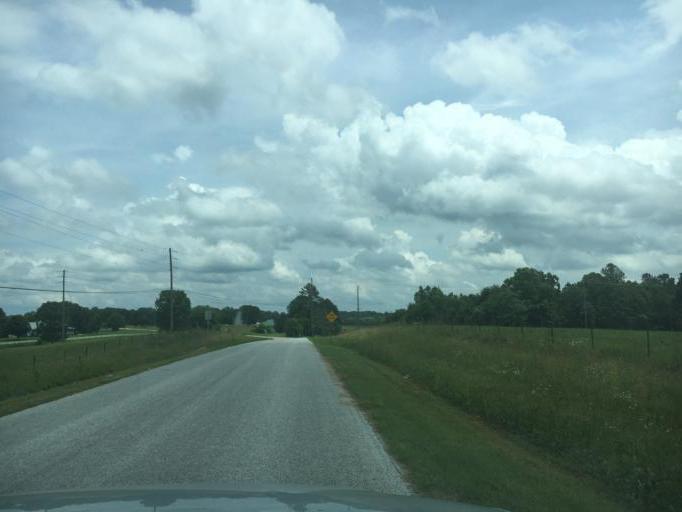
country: US
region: Georgia
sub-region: Franklin County
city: Gumlog
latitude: 34.4578
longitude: -83.0541
